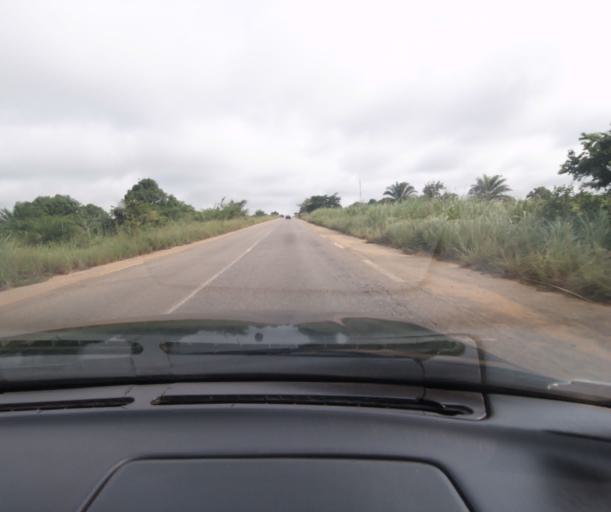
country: CM
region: Centre
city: Ombesa
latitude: 4.3997
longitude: 11.2502
